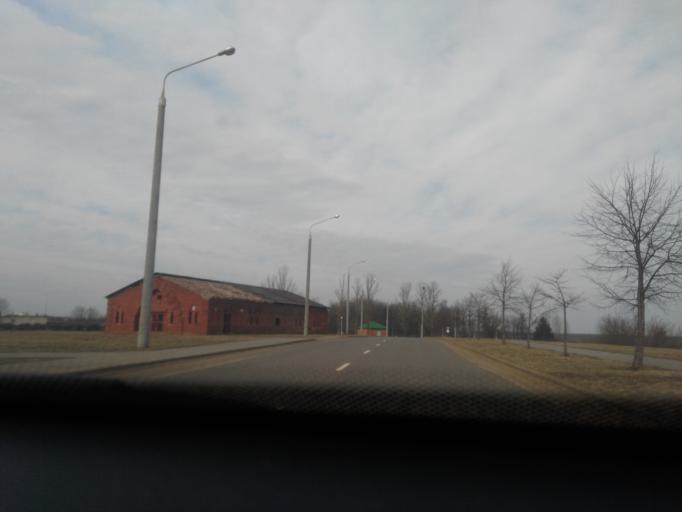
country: BY
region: Mogilev
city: Babruysk
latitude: 53.1433
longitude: 29.2513
